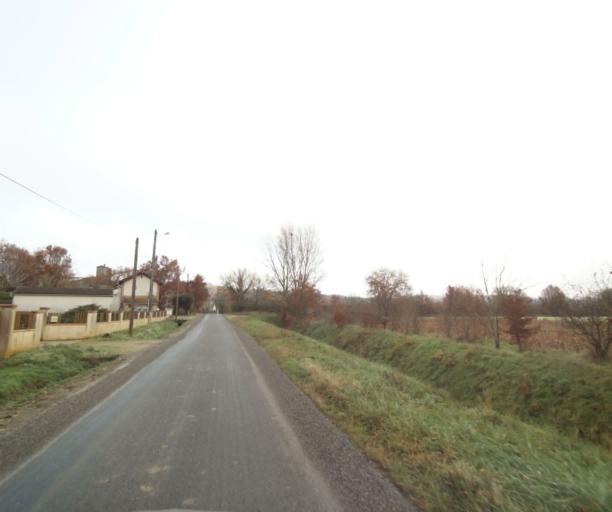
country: FR
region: Midi-Pyrenees
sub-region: Departement de la Haute-Garonne
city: Villemur-sur-Tarn
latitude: 43.8704
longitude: 1.4878
